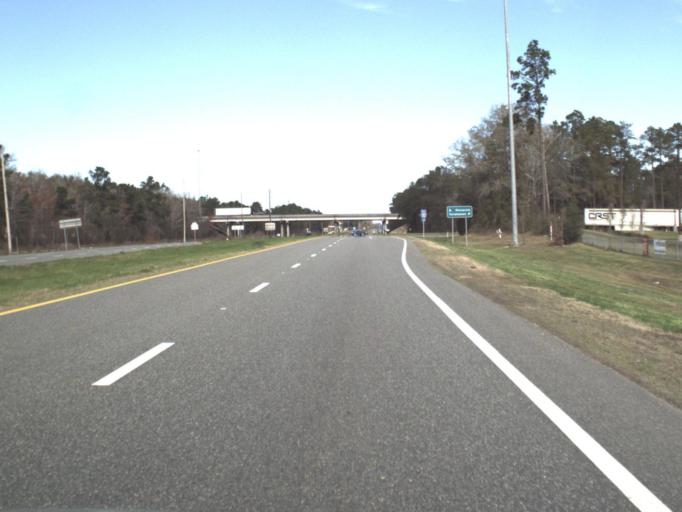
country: US
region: Florida
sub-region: Washington County
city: Chipley
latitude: 30.7490
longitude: -85.3835
